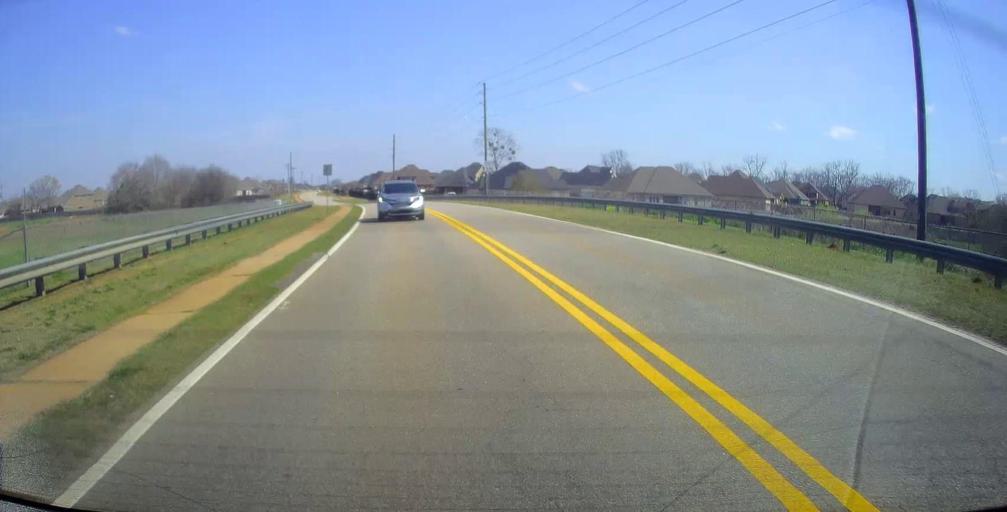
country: US
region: Georgia
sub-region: Houston County
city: Centerville
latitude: 32.5675
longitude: -83.7109
